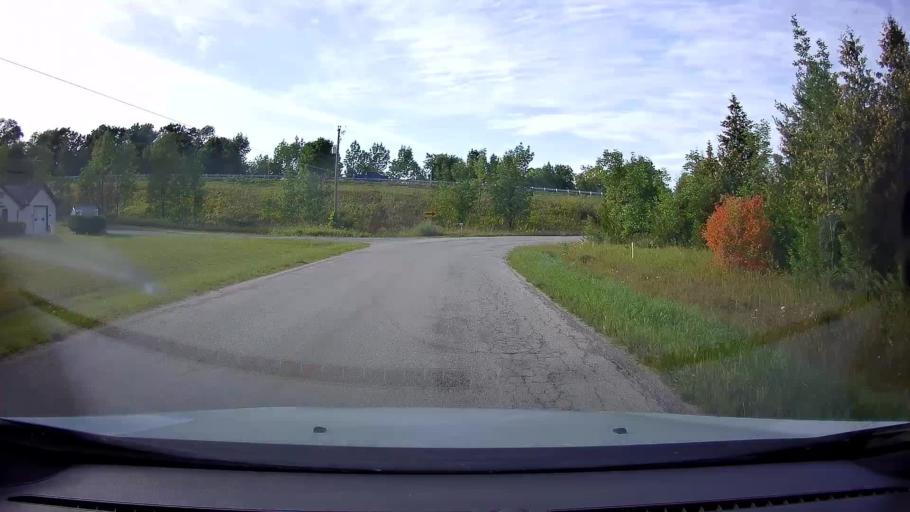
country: US
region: Wisconsin
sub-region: Door County
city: Sturgeon Bay
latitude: 45.1805
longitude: -87.1460
